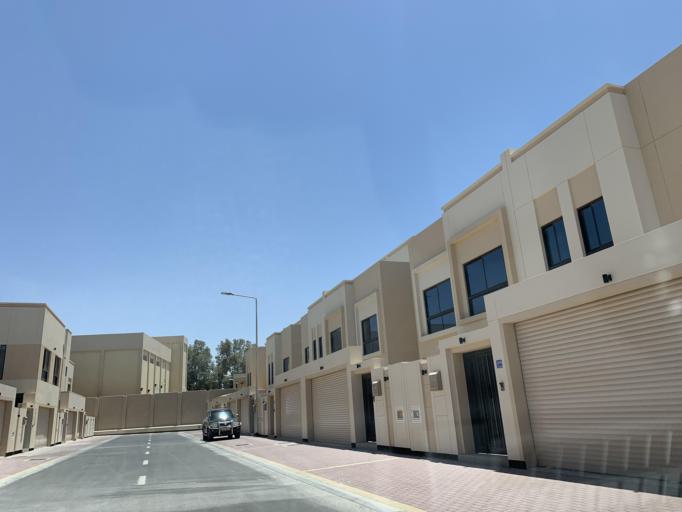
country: BH
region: Manama
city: Jidd Hafs
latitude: 26.2322
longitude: 50.4970
